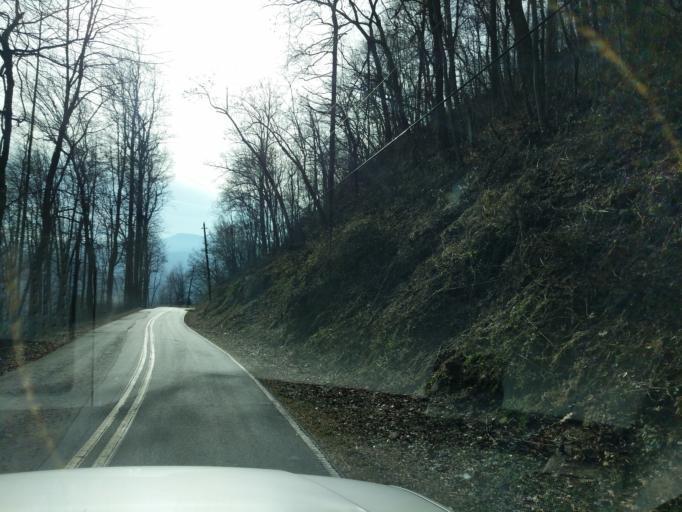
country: US
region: North Carolina
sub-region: Polk County
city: Columbus
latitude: 35.2718
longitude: -82.2117
